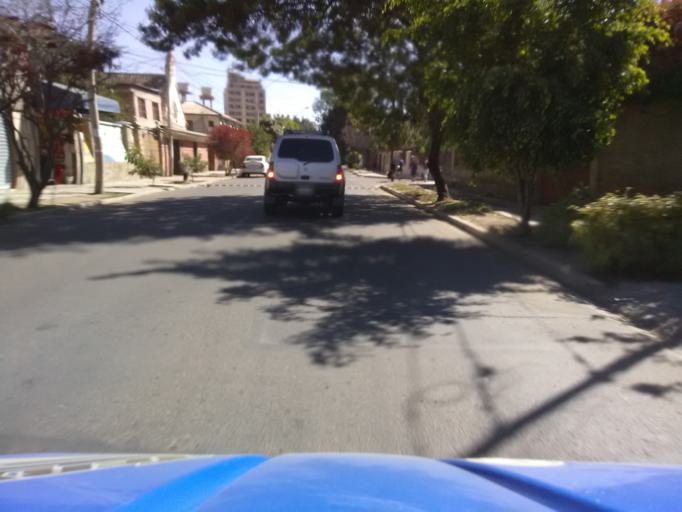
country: BO
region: Cochabamba
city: Cochabamba
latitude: -17.3969
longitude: -66.1461
